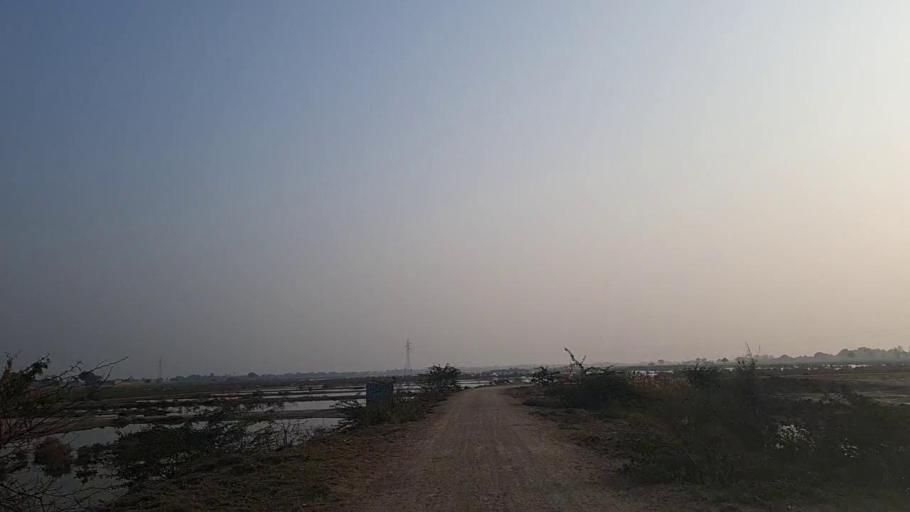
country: PK
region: Sindh
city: Nawabshah
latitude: 26.2365
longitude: 68.4710
